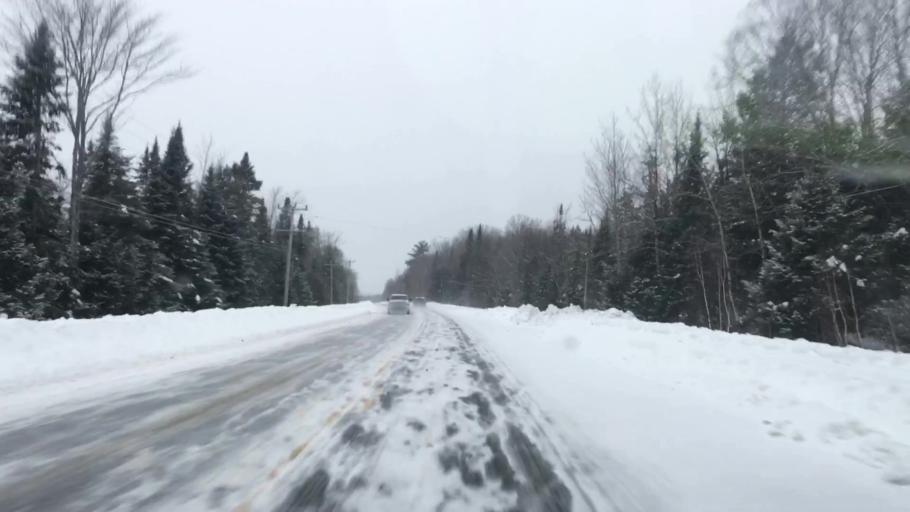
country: US
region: Maine
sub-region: Penobscot County
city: Medway
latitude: 45.5846
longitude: -68.4287
